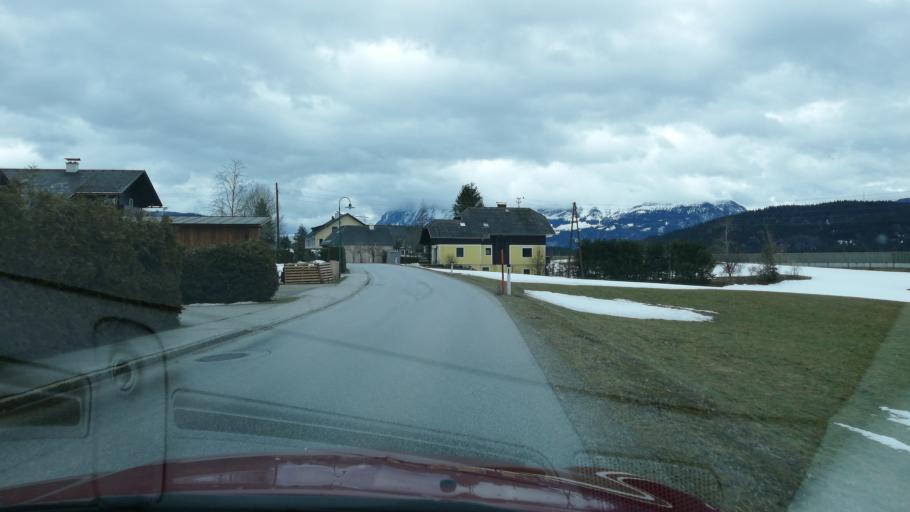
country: AT
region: Styria
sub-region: Politischer Bezirk Liezen
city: Bad Aussee
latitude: 47.5671
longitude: 13.8643
